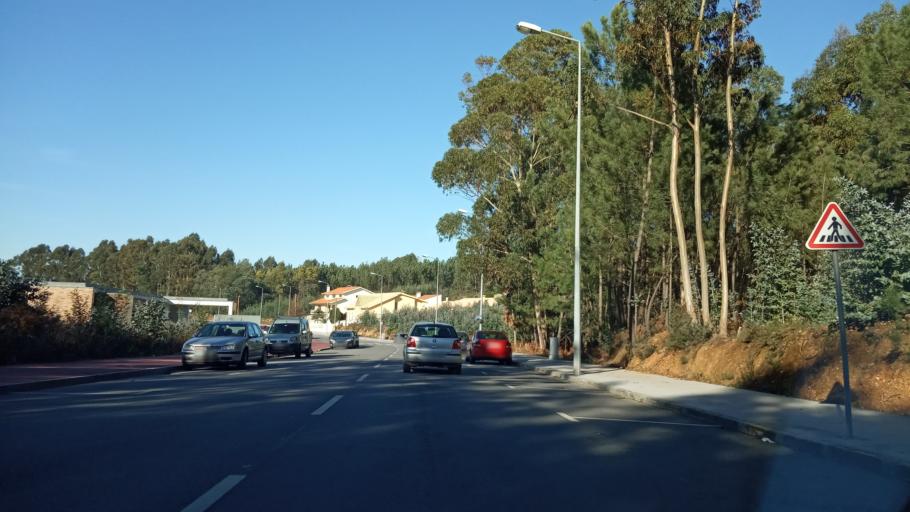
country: PT
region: Aveiro
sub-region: Anadia
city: Anadia
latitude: 40.4307
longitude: -8.4365
